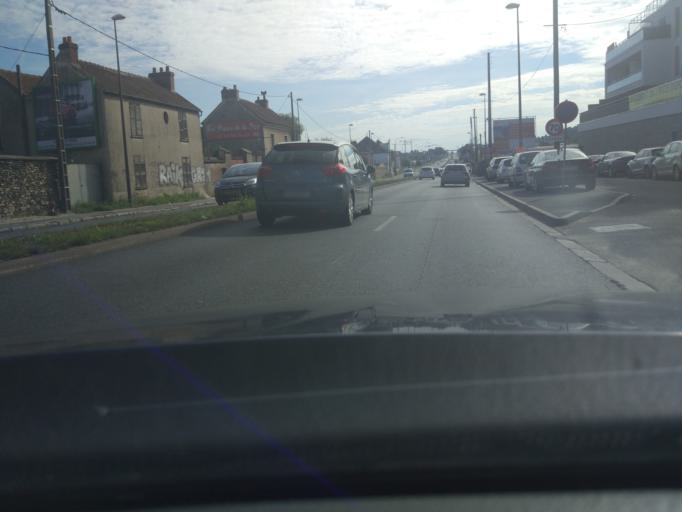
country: FR
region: Ile-de-France
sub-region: Departement de l'Essonne
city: La Ville-du-Bois
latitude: 48.6596
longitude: 2.2757
